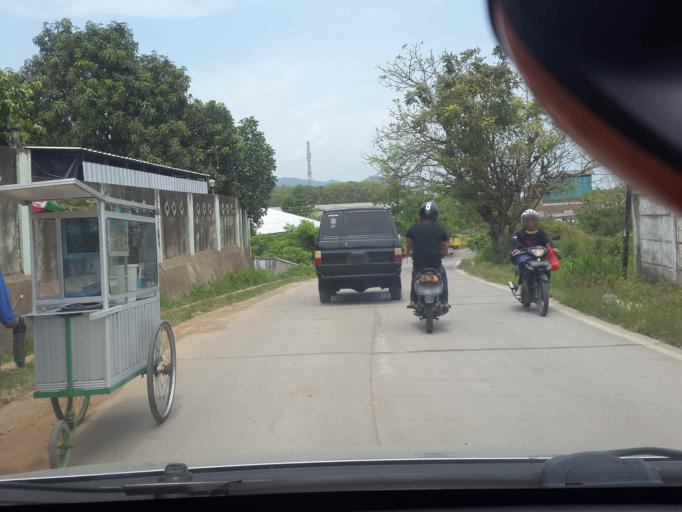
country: ID
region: Lampung
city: Panjang
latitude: -5.4413
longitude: 105.2998
